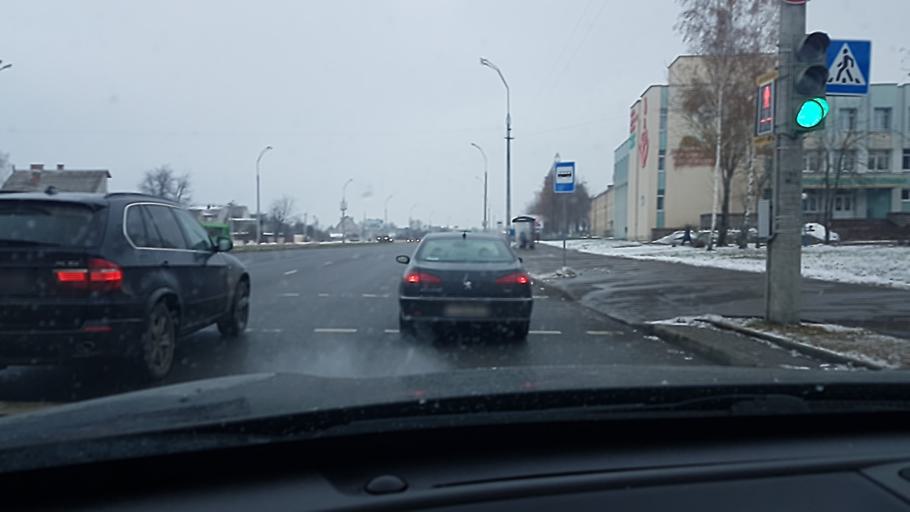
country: BY
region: Minsk
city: Bal'shavik
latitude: 53.9527
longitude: 27.5351
